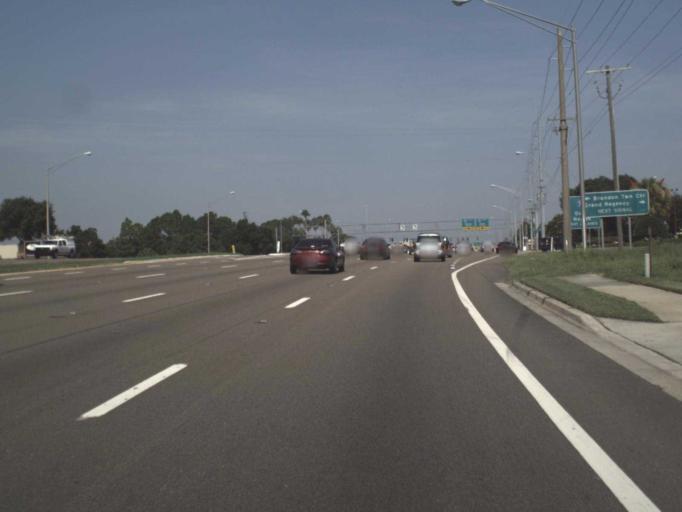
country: US
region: Florida
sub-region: Hillsborough County
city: Brandon
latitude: 27.9382
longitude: -82.3204
